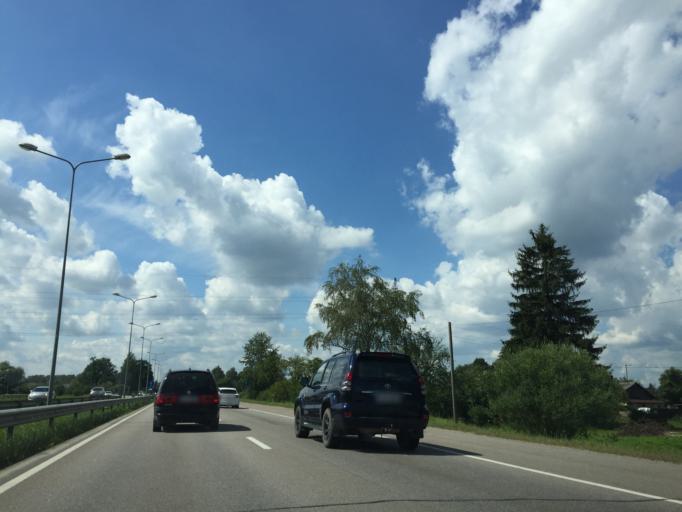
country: LV
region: Olaine
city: Olaine
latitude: 56.7890
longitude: 23.9592
